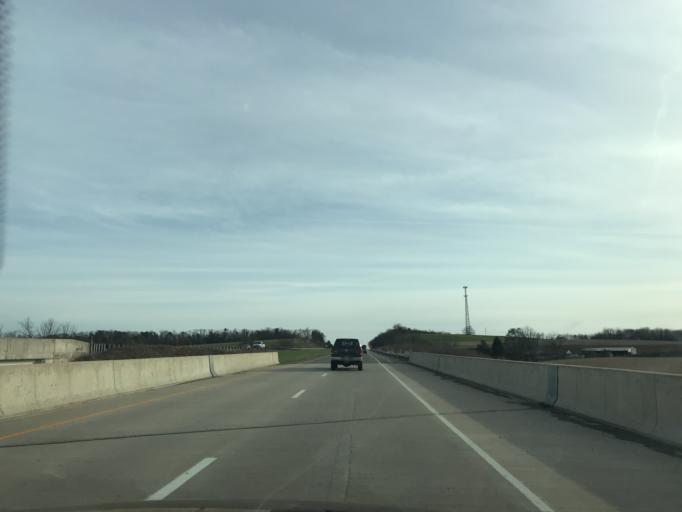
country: US
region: Pennsylvania
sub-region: Northumberland County
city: Watsontown
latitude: 41.0750
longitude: -76.8265
